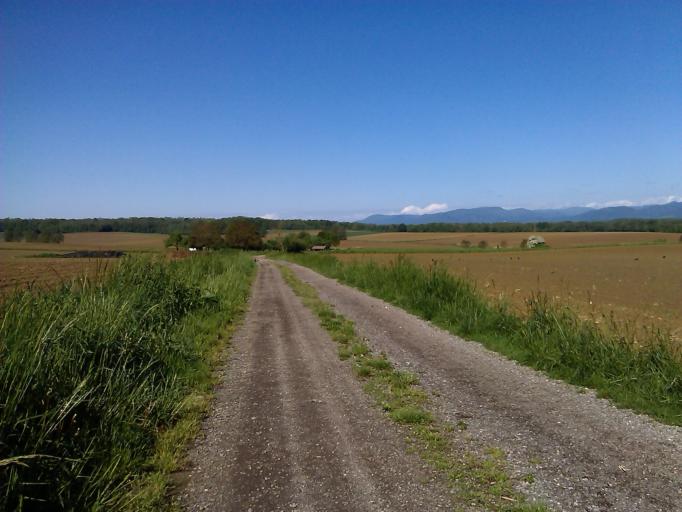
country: FR
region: Alsace
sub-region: Departement du Haut-Rhin
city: Heimsbrunn
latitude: 47.7151
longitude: 7.2293
